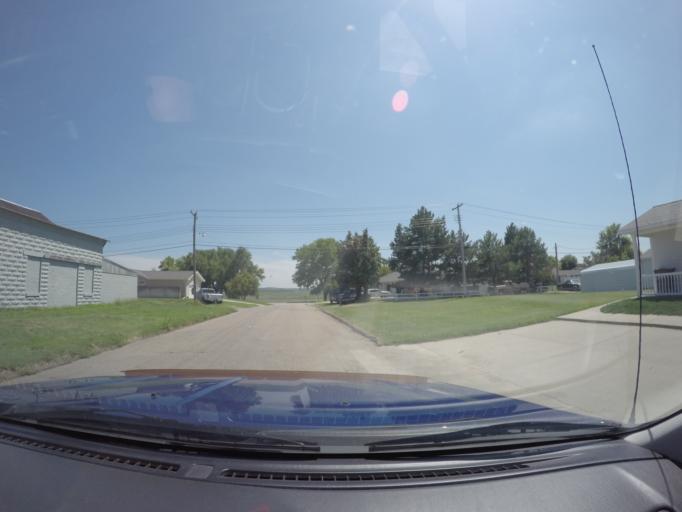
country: US
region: Nebraska
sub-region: Harlan County
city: Alma
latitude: 40.0971
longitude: -99.3647
